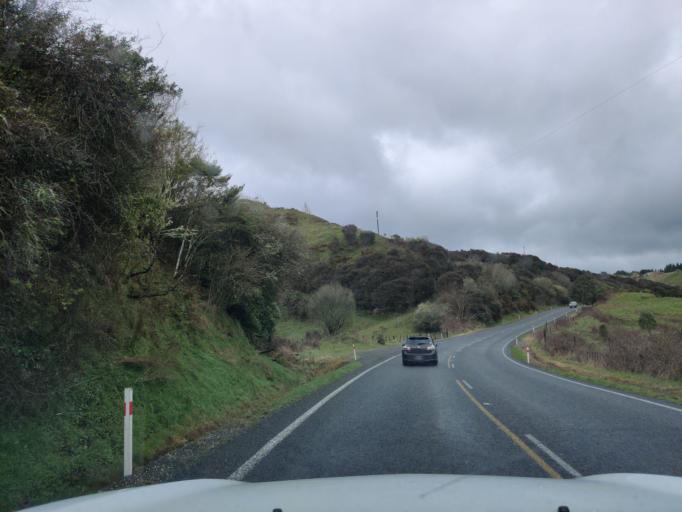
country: NZ
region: Waikato
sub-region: Otorohanga District
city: Otorohanga
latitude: -38.6274
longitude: 175.2127
